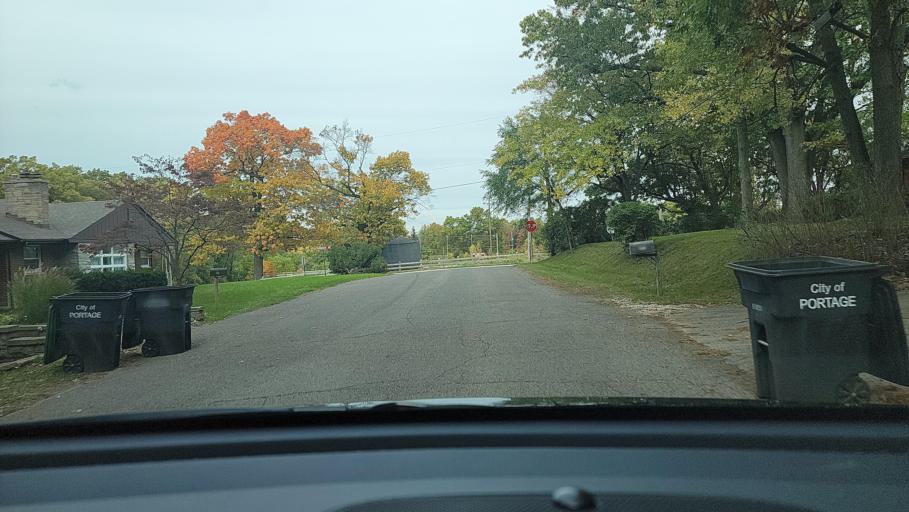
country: US
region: Indiana
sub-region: Porter County
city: Portage
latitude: 41.5790
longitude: -87.1892
